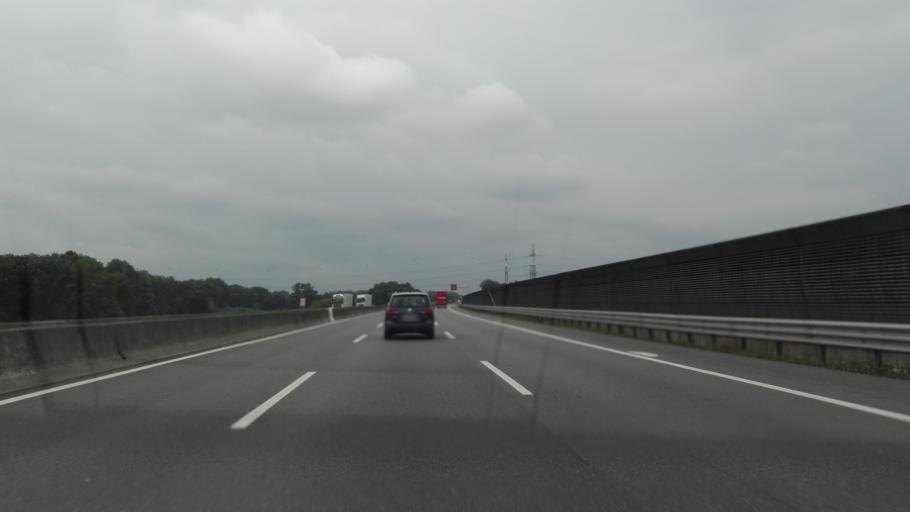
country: AT
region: Lower Austria
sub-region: Politischer Bezirk Melk
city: Neumarkt an der Ybbs
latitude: 48.1338
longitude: 15.0521
